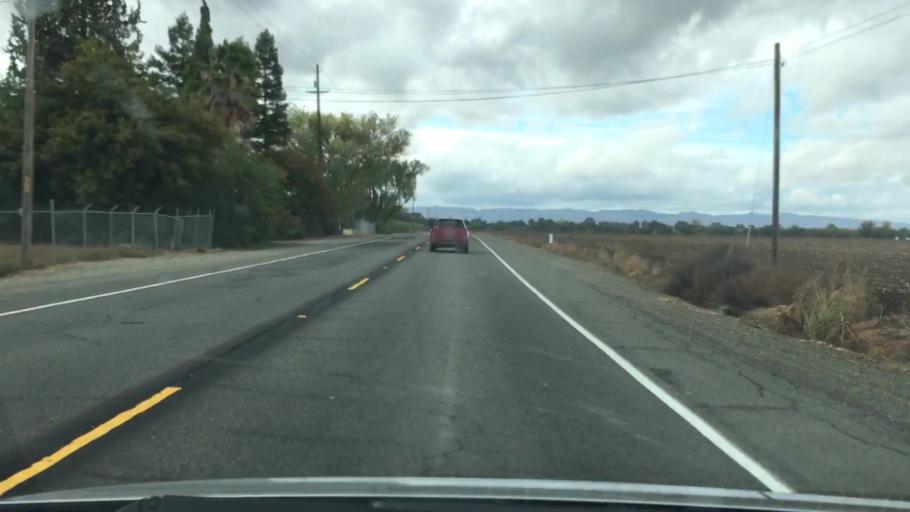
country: US
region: California
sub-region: Yolo County
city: Davis
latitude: 38.5616
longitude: -121.8311
